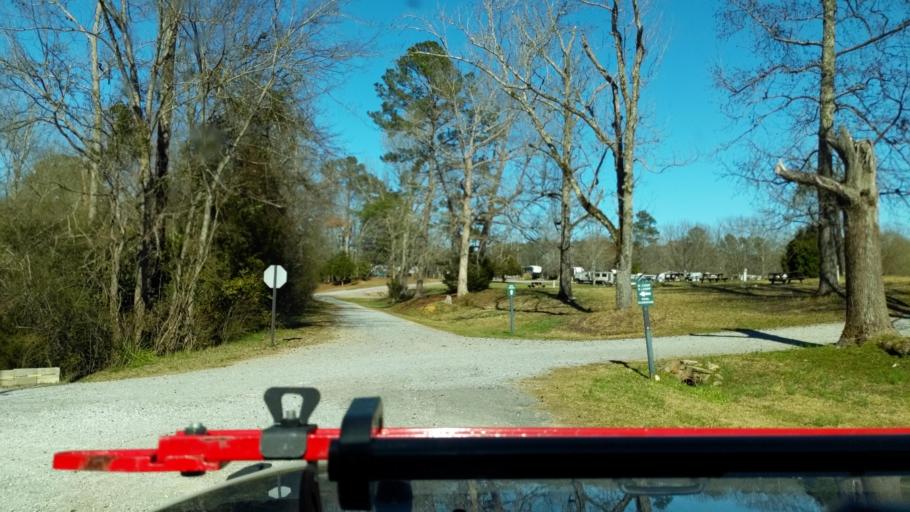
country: US
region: Alabama
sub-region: Walker County
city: Jasper
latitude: 34.0543
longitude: -87.1455
